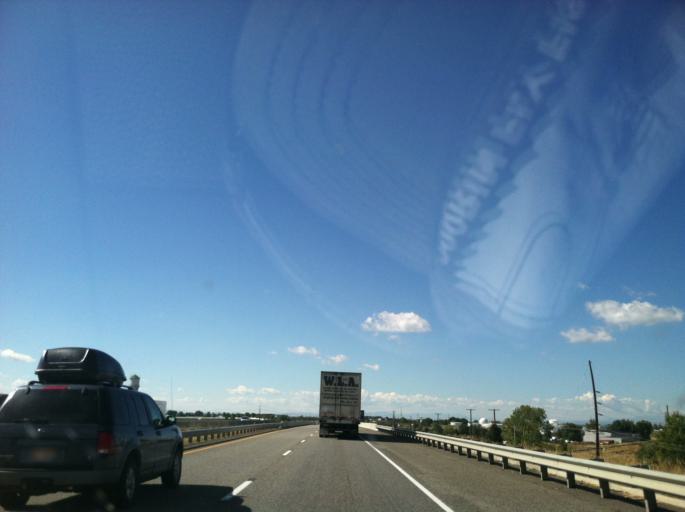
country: US
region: Montana
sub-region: Gallatin County
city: Bozeman
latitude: 45.6936
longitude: -111.0310
